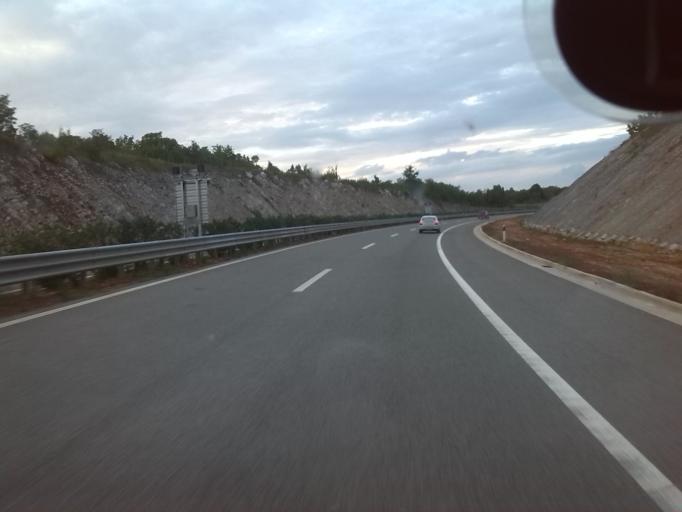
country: HR
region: Istarska
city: Buje
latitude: 45.4289
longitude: 13.6118
